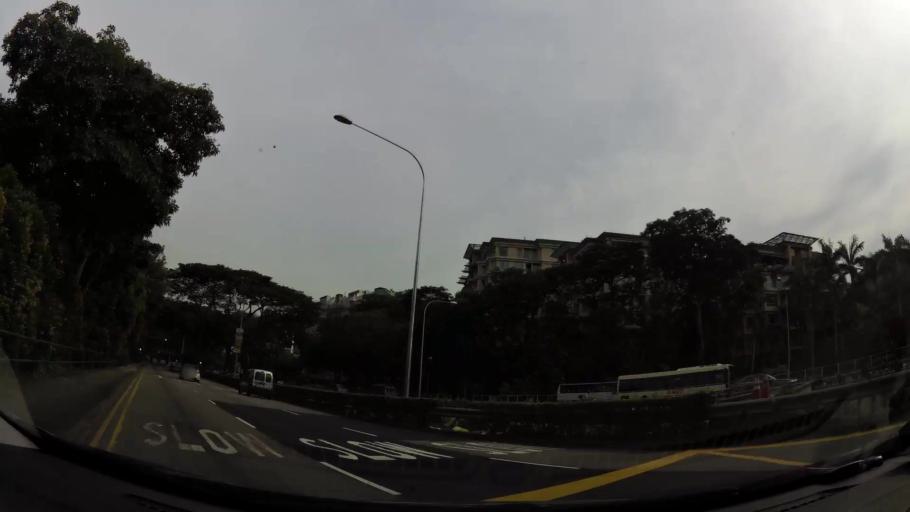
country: SG
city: Singapore
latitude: 1.3354
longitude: 103.7855
